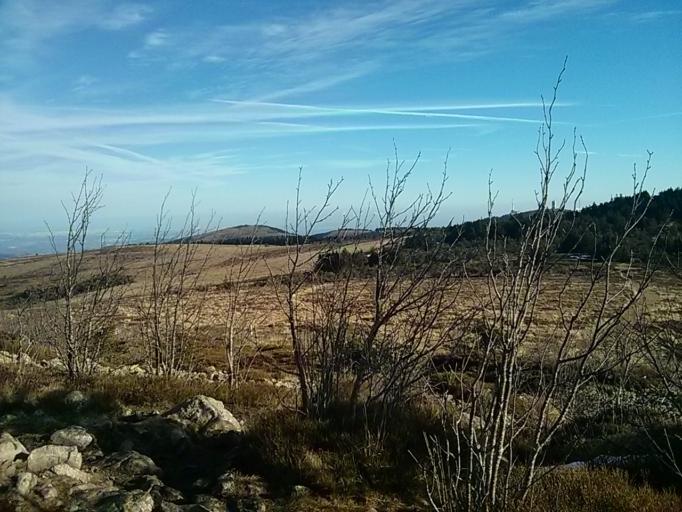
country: FR
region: Rhone-Alpes
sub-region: Departement de la Loire
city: Saint-Julien-Molin-Molette
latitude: 45.3825
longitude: 4.5733
